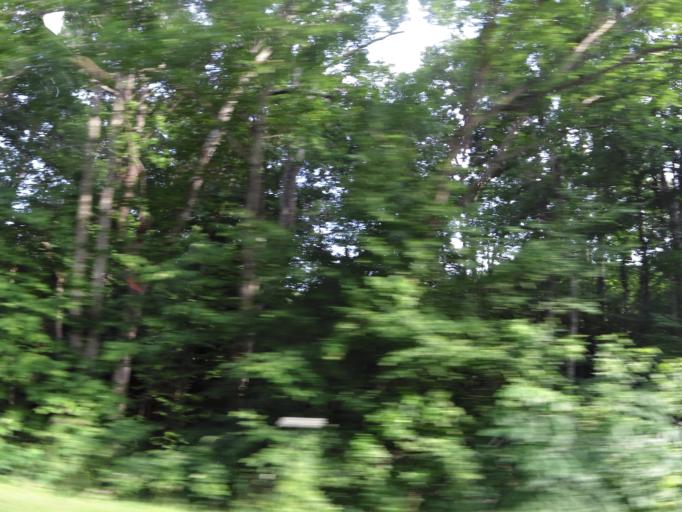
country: US
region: Tennessee
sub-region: Humphreys County
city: McEwen
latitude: 36.1027
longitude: -87.6614
